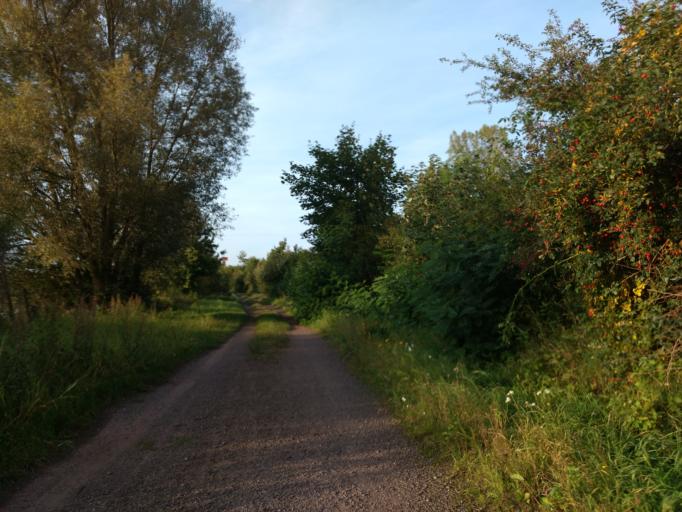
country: DE
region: Saarland
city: Ensdorf
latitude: 49.3165
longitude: 6.7741
